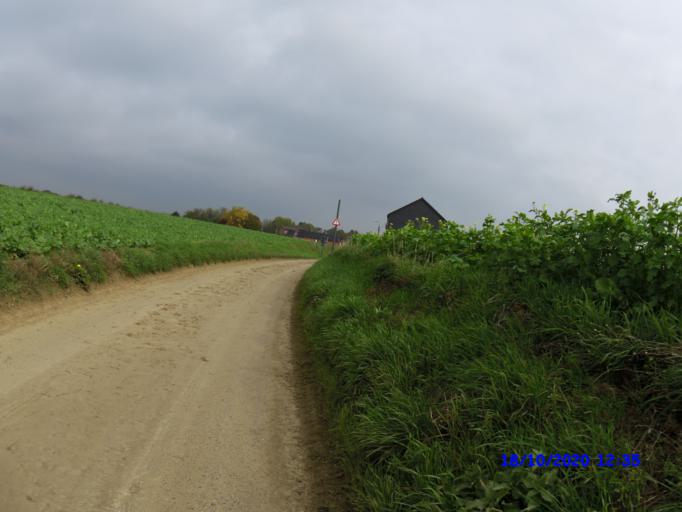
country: BE
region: Wallonia
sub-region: Province de Liege
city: Lincent
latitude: 50.7611
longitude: 5.0330
